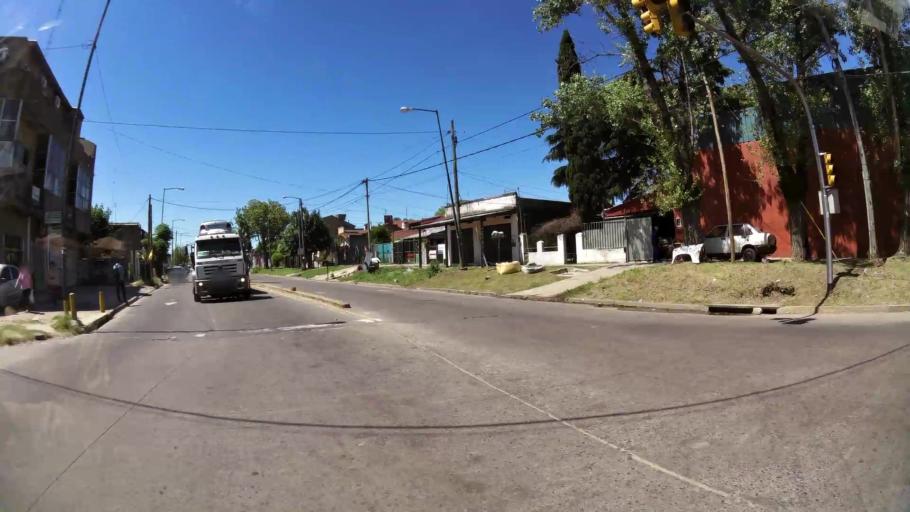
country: AR
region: Buenos Aires
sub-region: Partido de Tigre
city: Tigre
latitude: -34.4995
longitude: -58.5830
